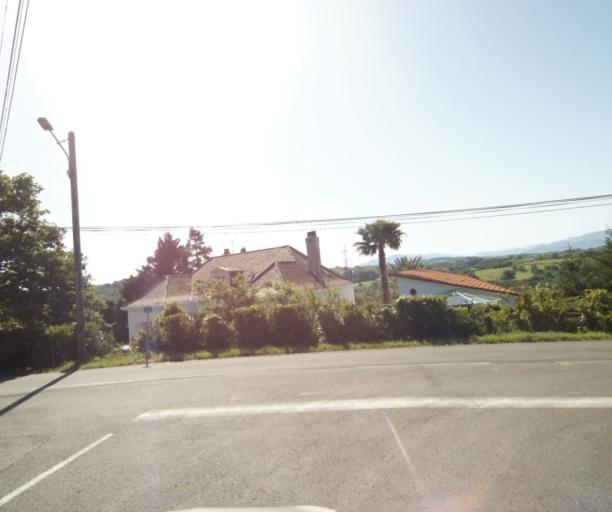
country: FR
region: Aquitaine
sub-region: Departement des Pyrenees-Atlantiques
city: Villefranque
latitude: 43.4549
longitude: -1.4390
